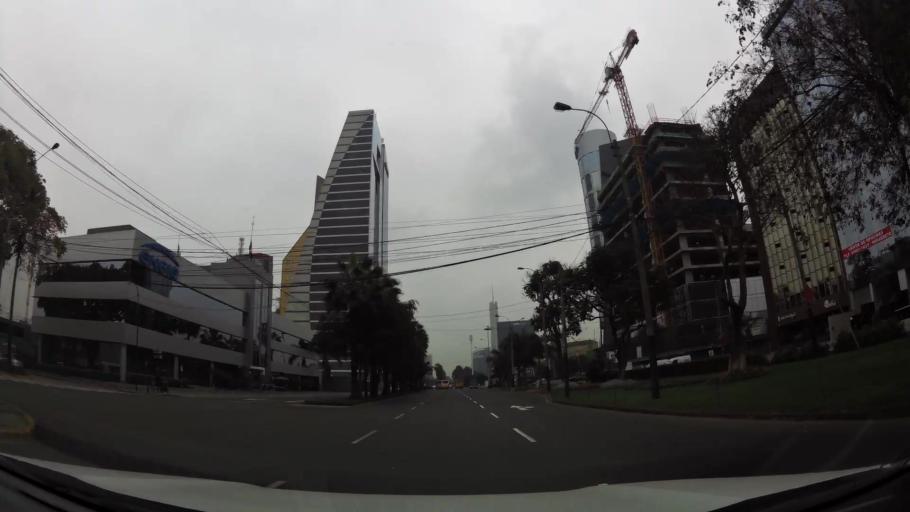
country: PE
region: Lima
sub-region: Lima
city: San Luis
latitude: -12.0991
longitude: -77.0198
